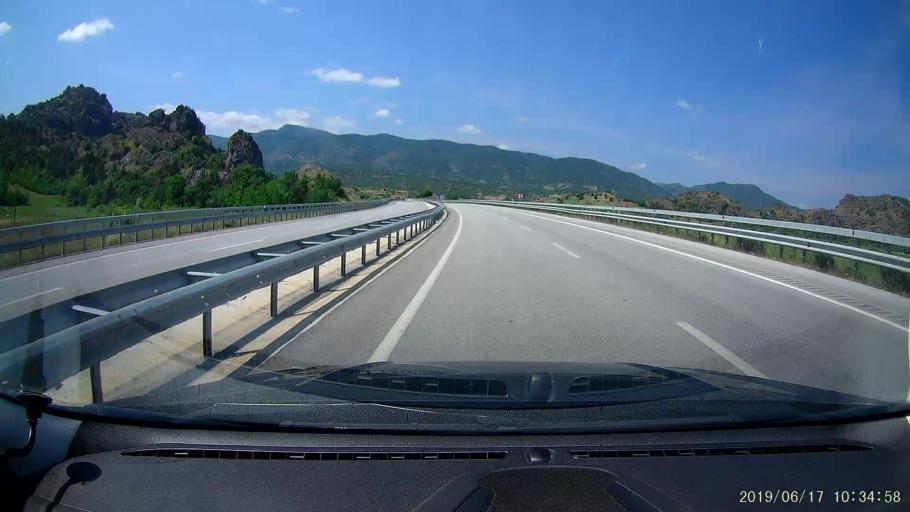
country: TR
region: Corum
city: Osmancik
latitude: 40.9795
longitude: 34.7125
